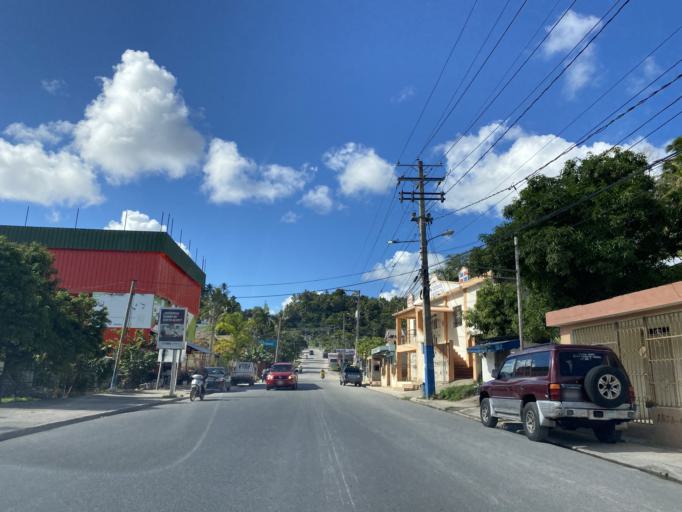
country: DO
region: Samana
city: Samana
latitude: 19.2060
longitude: -69.3471
